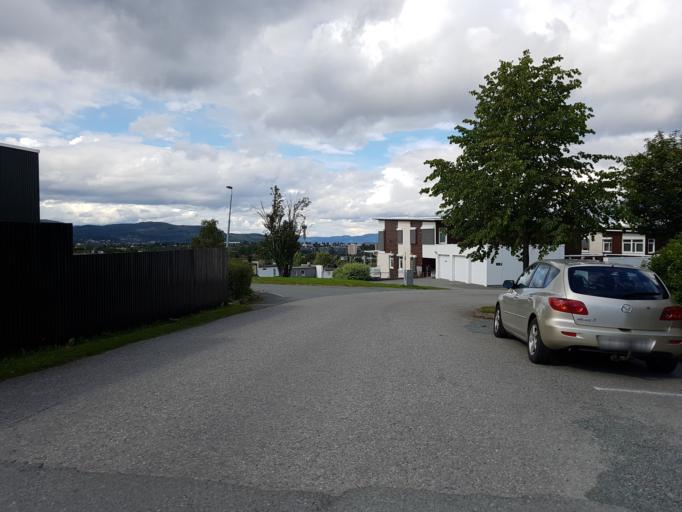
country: NO
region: Sor-Trondelag
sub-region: Trondheim
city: Trondheim
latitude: 63.4132
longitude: 10.4658
